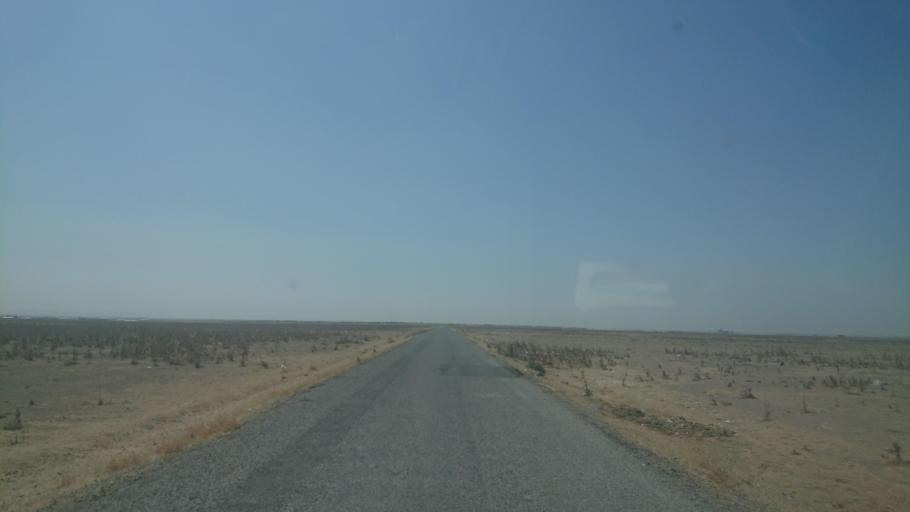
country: TR
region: Aksaray
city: Yesilova
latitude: 38.3245
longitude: 33.7457
